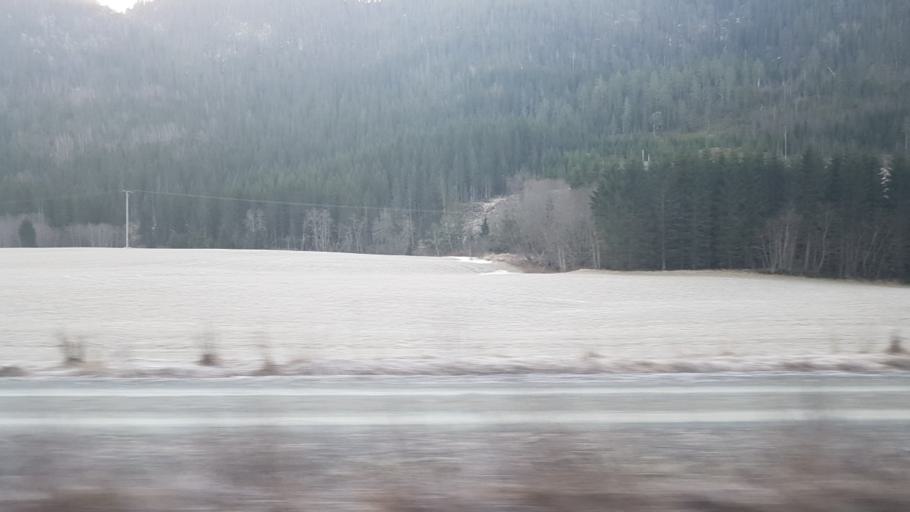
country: NO
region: Nord-Trondelag
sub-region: Stjordal
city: Stjordalshalsen
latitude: 63.5911
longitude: 11.0138
